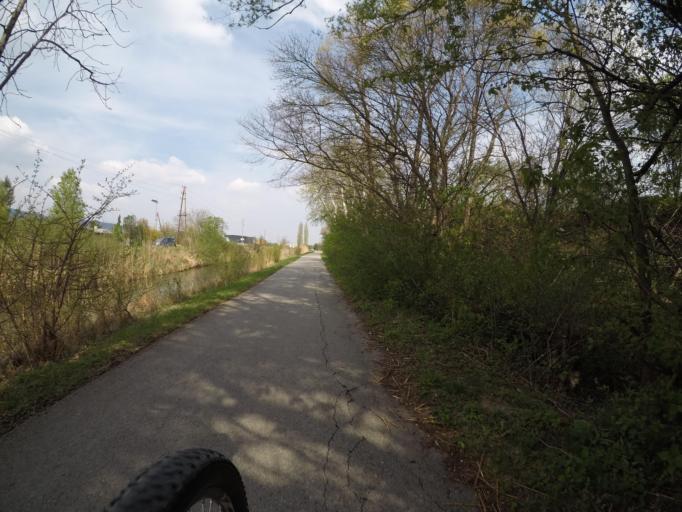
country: AT
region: Lower Austria
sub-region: Politischer Bezirk Baden
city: Traiskirchen
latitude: 48.0272
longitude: 16.2830
